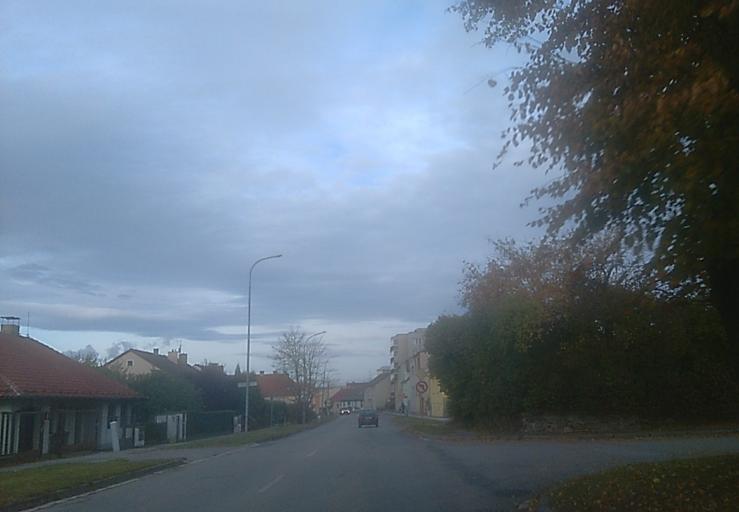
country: CZ
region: Jihocesky
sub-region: Okres Ceske Budejovice
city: Ceske Budejovice
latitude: 48.9716
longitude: 14.5107
